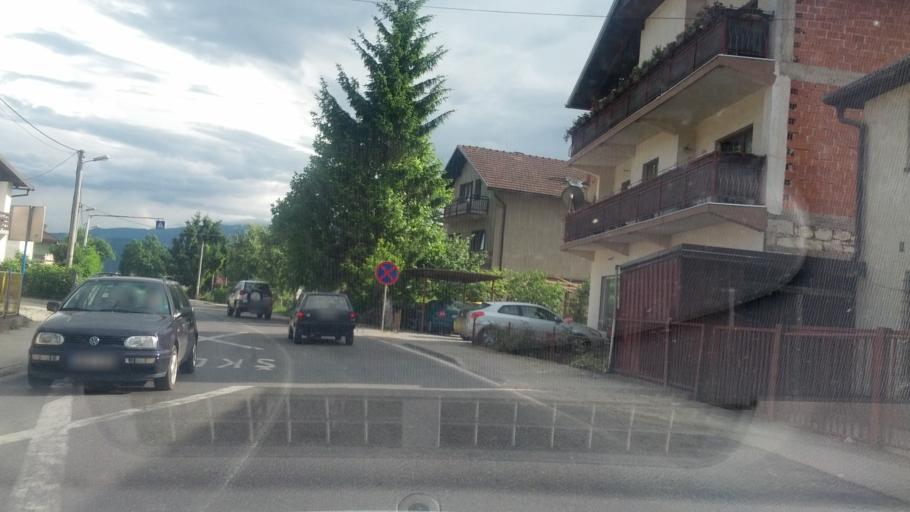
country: BA
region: Federation of Bosnia and Herzegovina
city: Bihac
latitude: 44.8563
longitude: 15.8823
